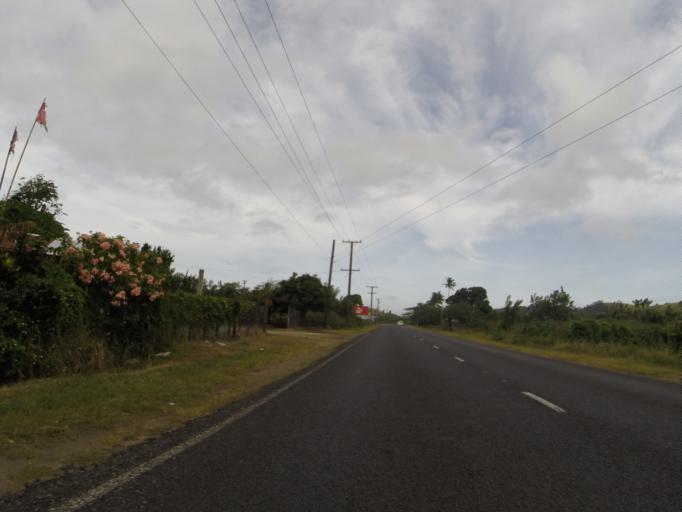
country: FJ
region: Western
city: Nadi
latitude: -18.1548
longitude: 177.4949
